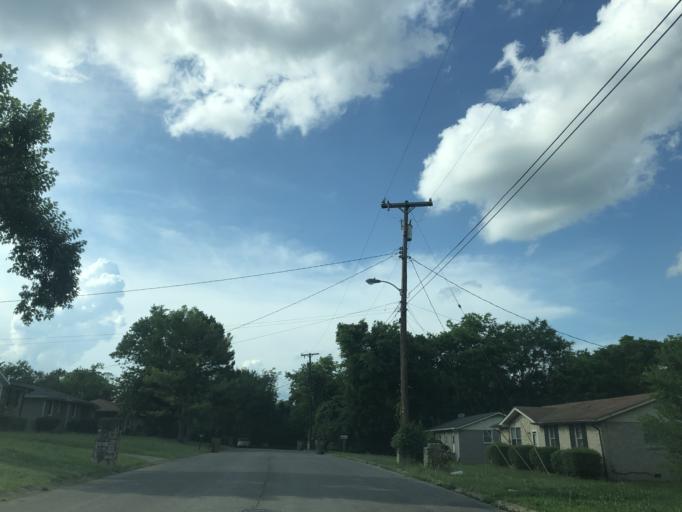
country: US
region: Tennessee
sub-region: Davidson County
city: Nashville
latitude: 36.2287
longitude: -86.8251
